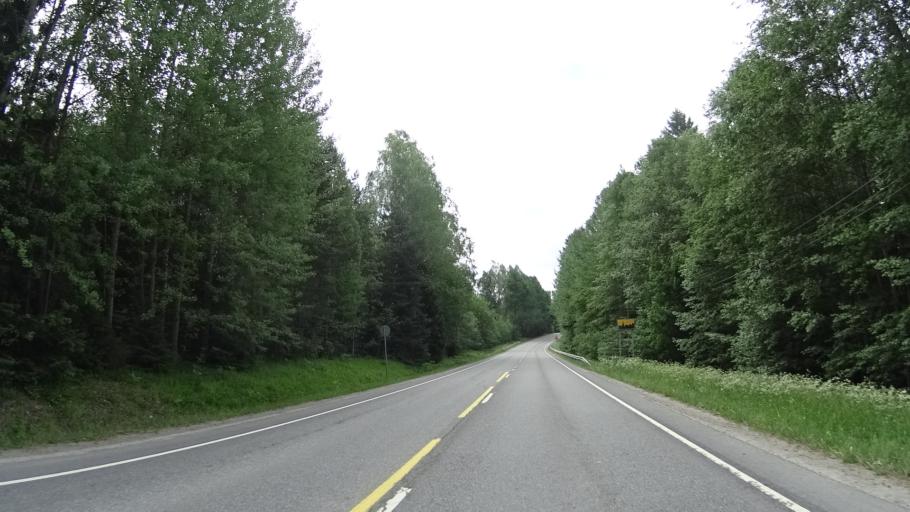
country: FI
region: Uusimaa
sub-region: Helsinki
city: Vihti
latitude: 60.2858
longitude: 24.4072
